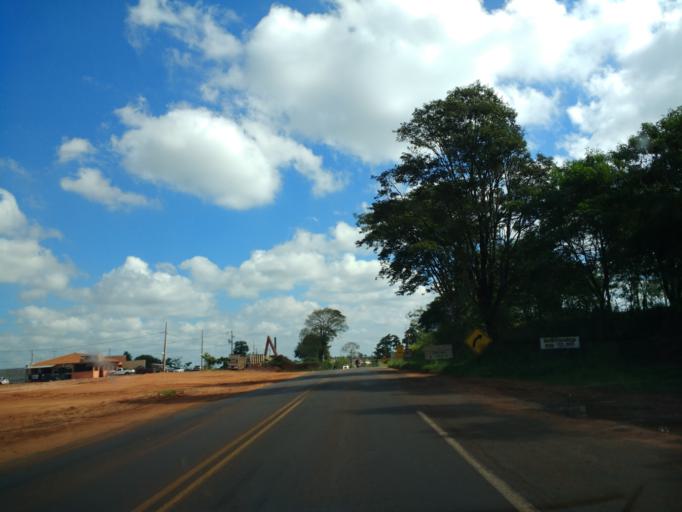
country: BR
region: Parana
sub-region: Alto Piquiri
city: Alto Piquiri
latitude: -23.8886
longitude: -53.4059
